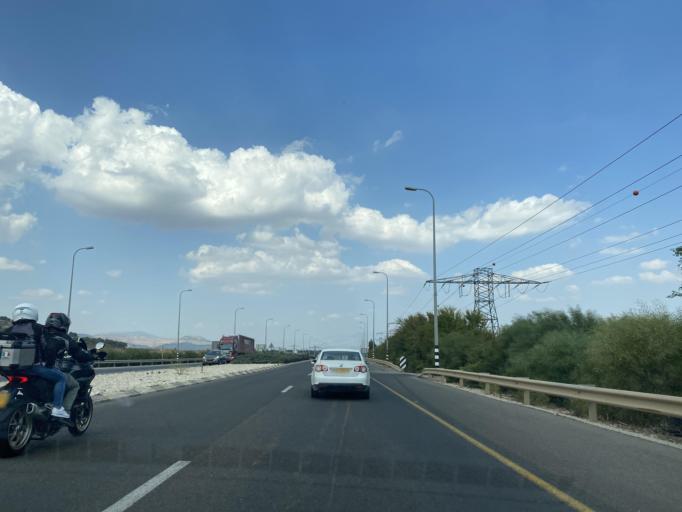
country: IL
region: Northern District
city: Rosh Pinna
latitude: 32.9827
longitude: 35.5581
